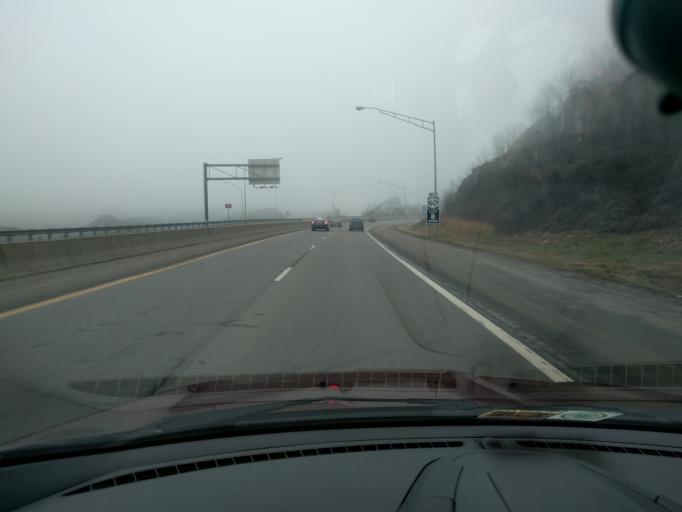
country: US
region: West Virginia
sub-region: Kanawha County
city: Chesapeake
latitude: 38.2002
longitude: -81.4964
